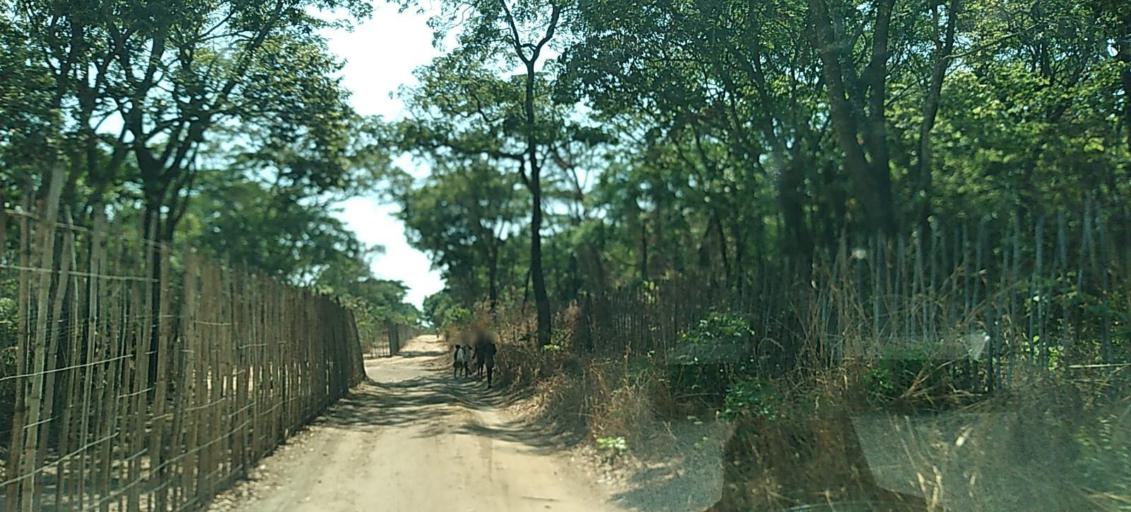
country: ZM
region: Copperbelt
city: Luanshya
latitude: -13.0093
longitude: 28.4680
